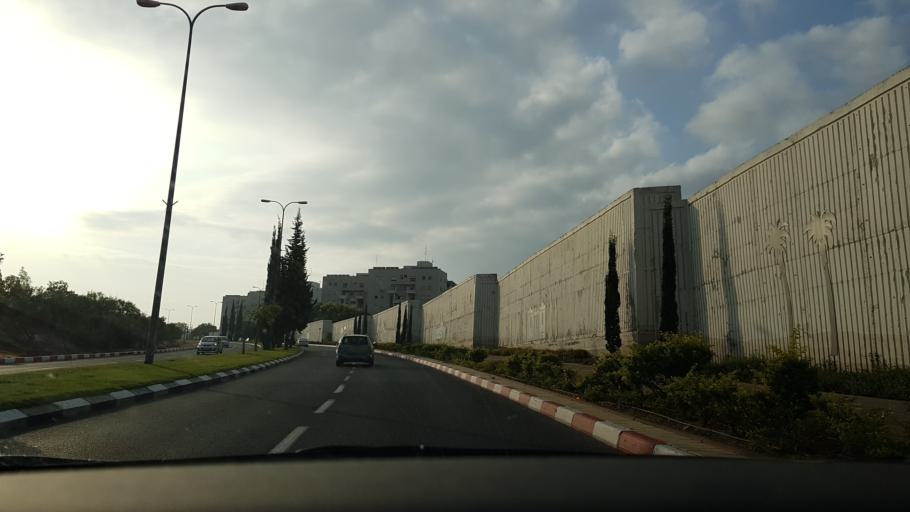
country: IL
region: Central District
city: Mazkeret Batya
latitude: 31.8934
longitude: 34.8277
